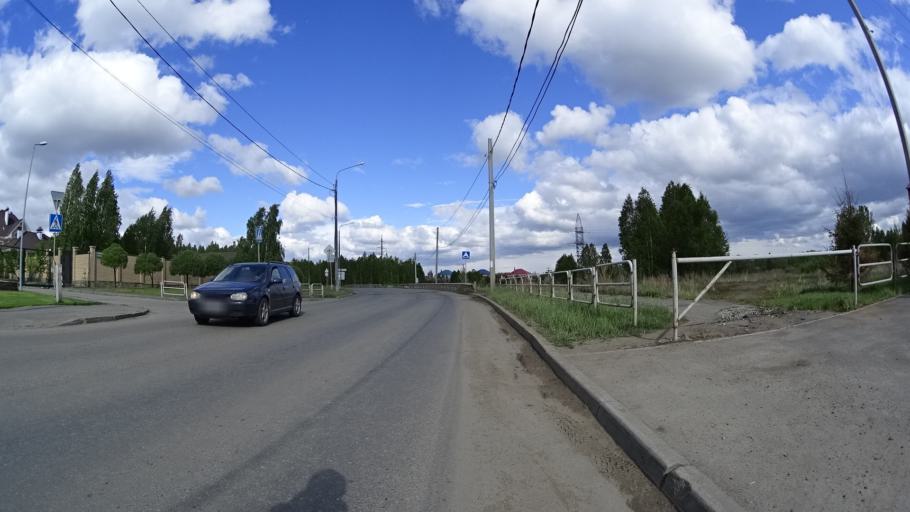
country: RU
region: Chelyabinsk
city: Sargazy
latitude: 55.1522
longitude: 61.2616
